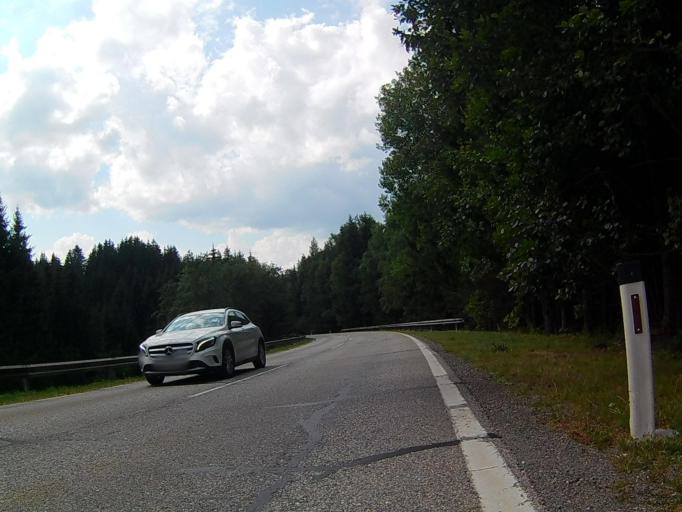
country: AT
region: Styria
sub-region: Politischer Bezirk Deutschlandsberg
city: Soboth
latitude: 46.6831
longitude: 15.0941
